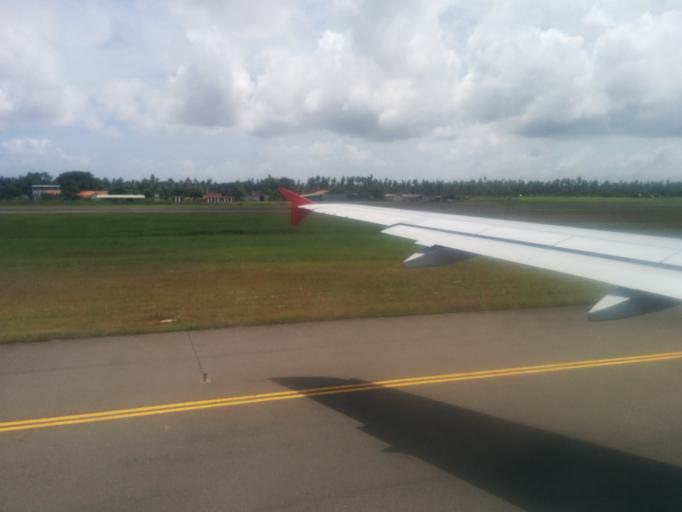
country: LK
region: Western
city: Katunayaka
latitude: 7.1812
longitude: 79.8861
